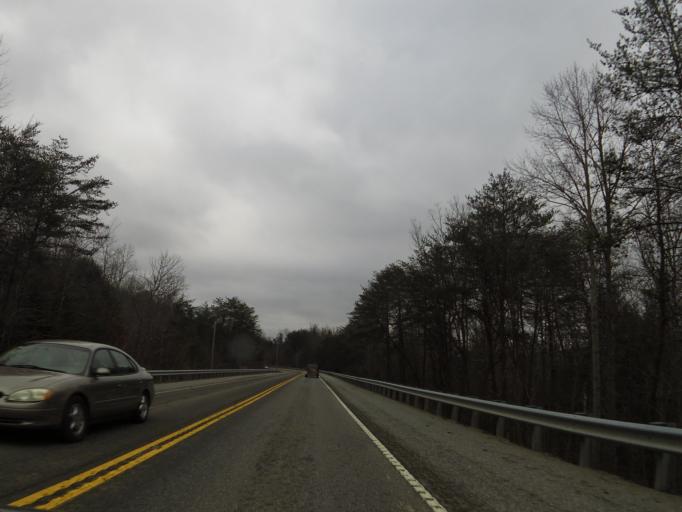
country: US
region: Tennessee
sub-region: Campbell County
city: Jacksboro
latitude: 36.3934
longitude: -84.2645
